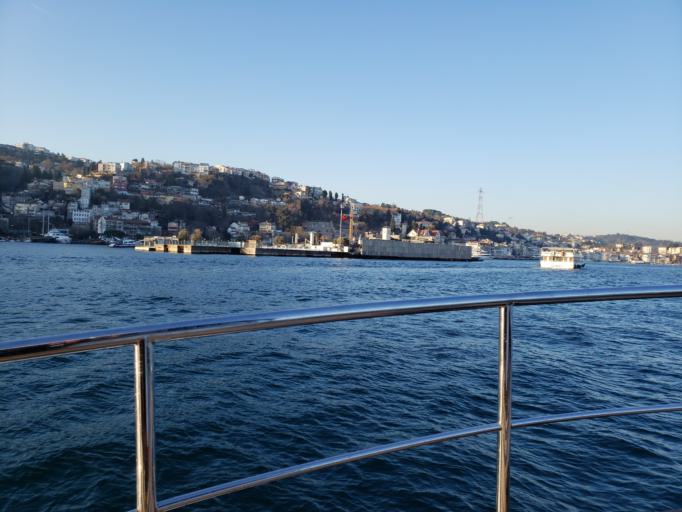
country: TR
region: Istanbul
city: UEskuedar
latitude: 41.0579
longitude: 29.0400
